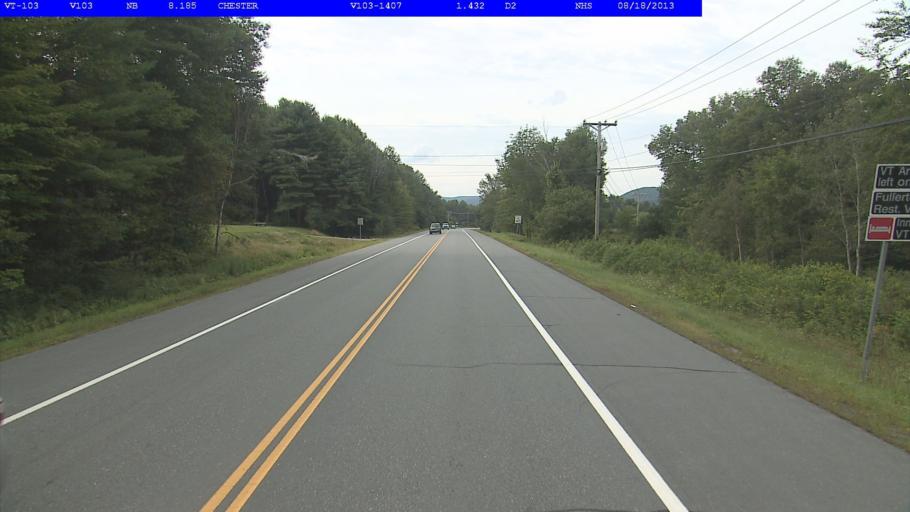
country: US
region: Vermont
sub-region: Windsor County
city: Chester
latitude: 43.2486
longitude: -72.5744
